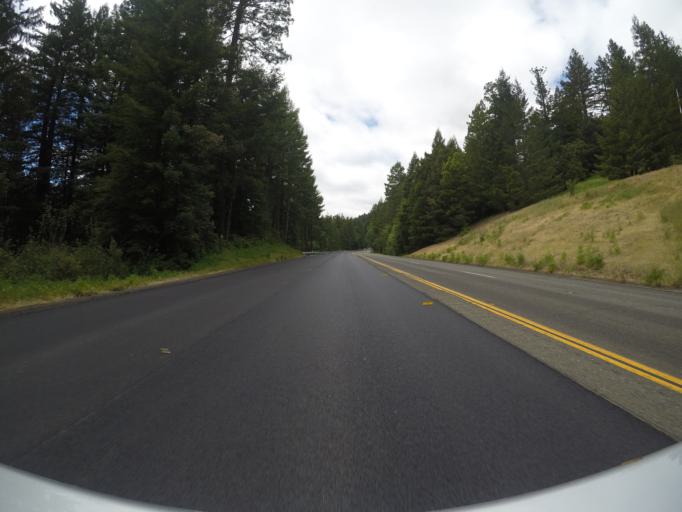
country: US
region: California
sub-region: Humboldt County
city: Redway
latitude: 40.3075
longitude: -123.9039
